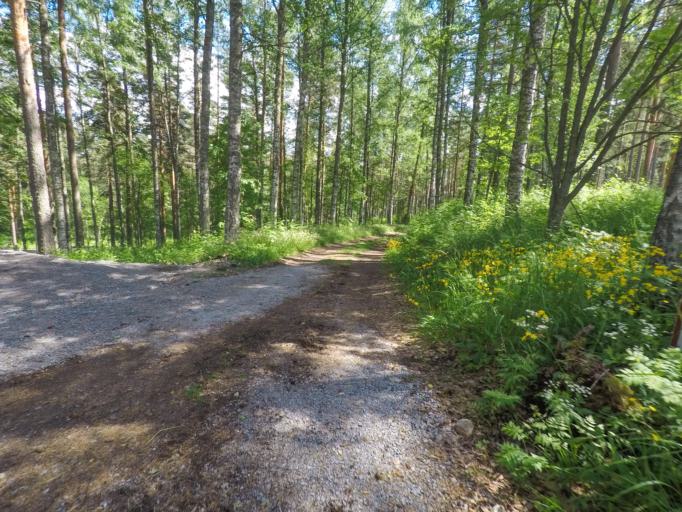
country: FI
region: Southern Savonia
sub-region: Savonlinna
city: Punkaharju
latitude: 61.8002
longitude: 29.3085
